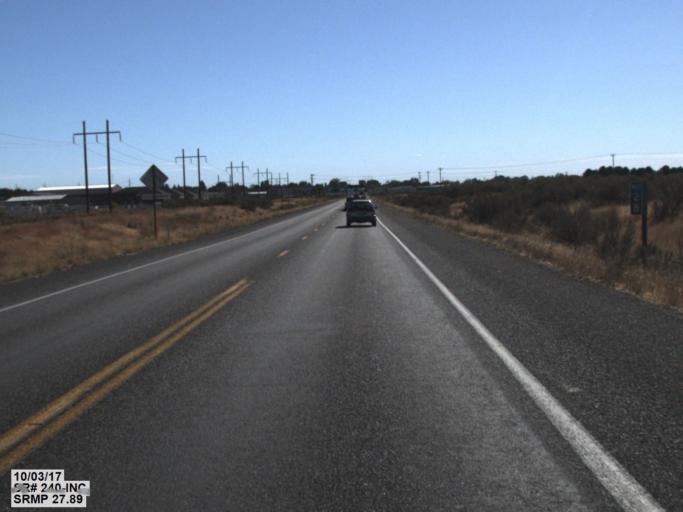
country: US
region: Washington
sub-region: Benton County
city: Richland
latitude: 46.3174
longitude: -119.3002
